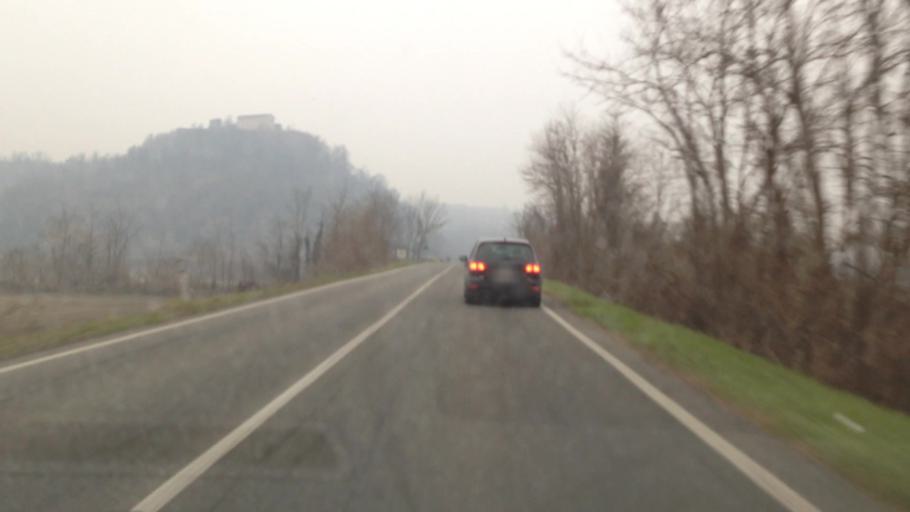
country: IT
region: Piedmont
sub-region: Provincia di Vercelli
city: Crescentino
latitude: 45.1810
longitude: 8.1001
